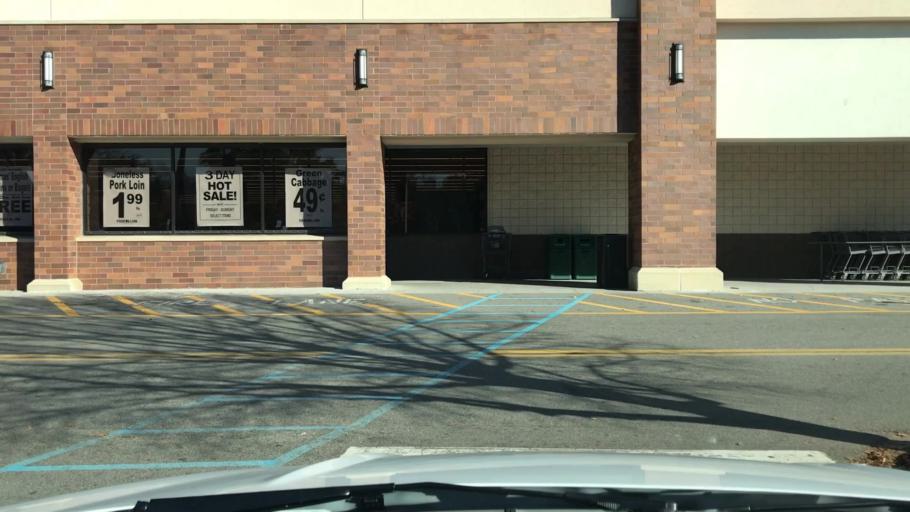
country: US
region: South Carolina
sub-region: Charleston County
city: Shell Point
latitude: 32.8135
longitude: -80.0410
